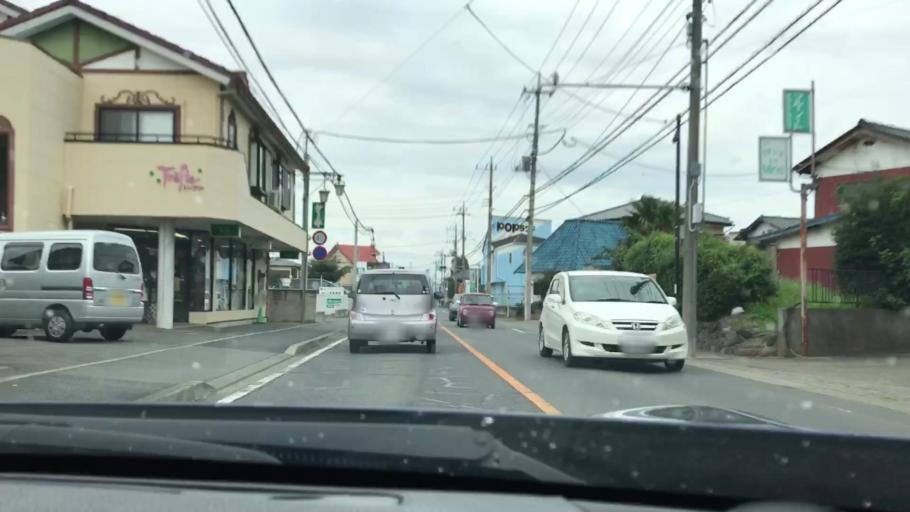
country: JP
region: Gunma
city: Takasaki
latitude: 36.3489
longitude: 139.0224
